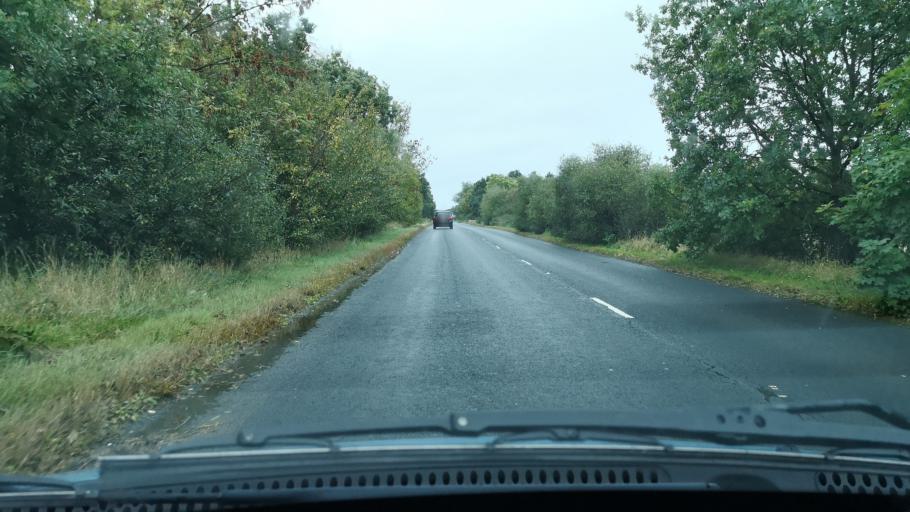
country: GB
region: England
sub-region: Doncaster
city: Hatfield
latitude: 53.5977
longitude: -0.9654
